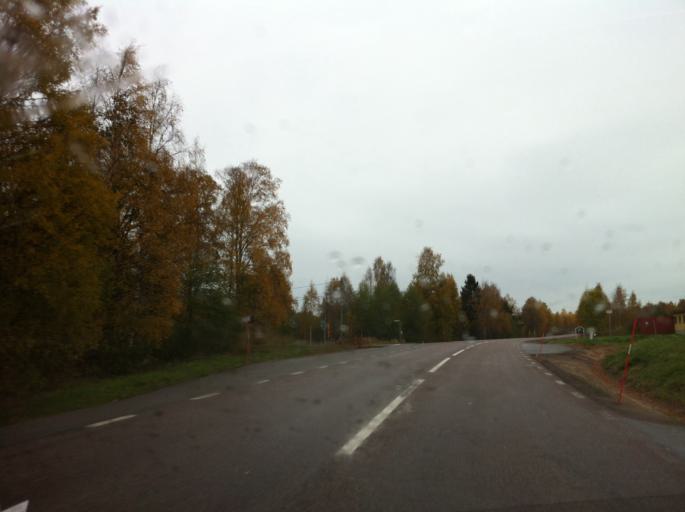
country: SE
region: Dalarna
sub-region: Ludvika Kommun
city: Grangesberg
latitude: 60.2398
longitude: 14.9848
